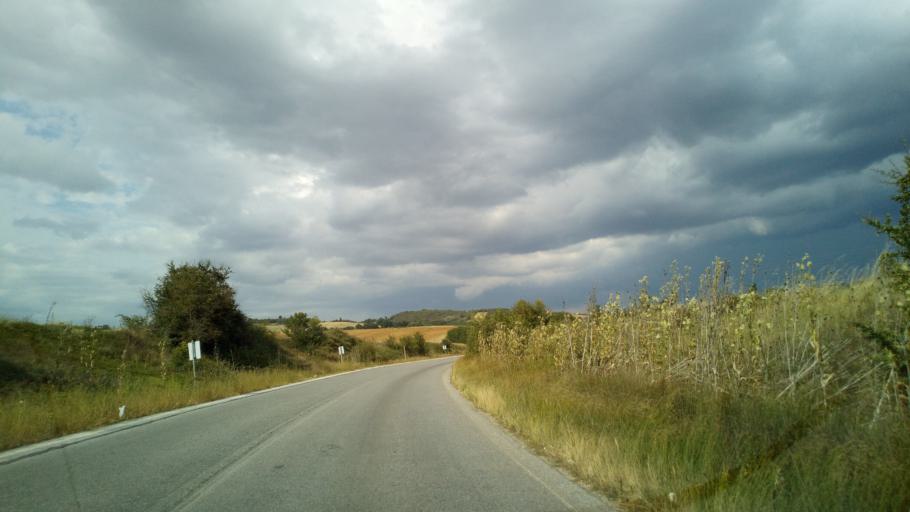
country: GR
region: Central Macedonia
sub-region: Nomos Chalkidikis
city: Polygyros
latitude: 40.4726
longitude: 23.3930
